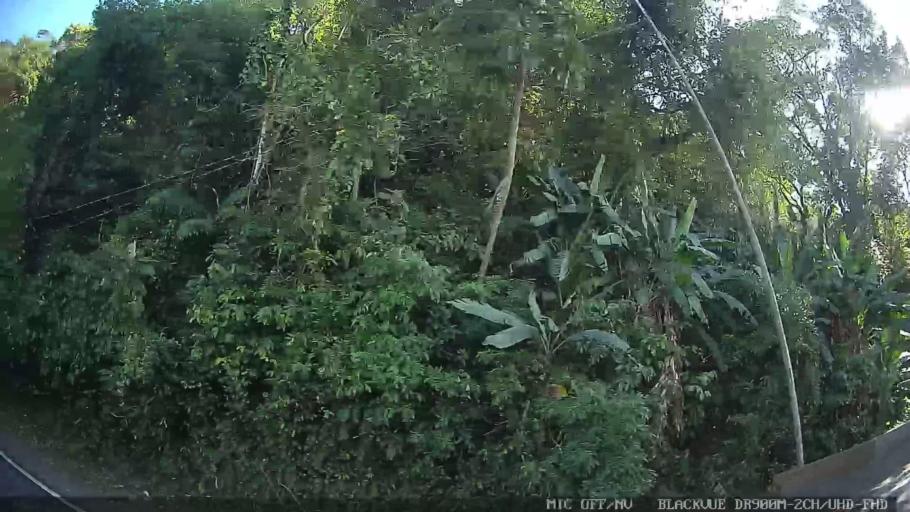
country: BR
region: Sao Paulo
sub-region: Cubatao
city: Cubatao
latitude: -23.8924
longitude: -46.4833
